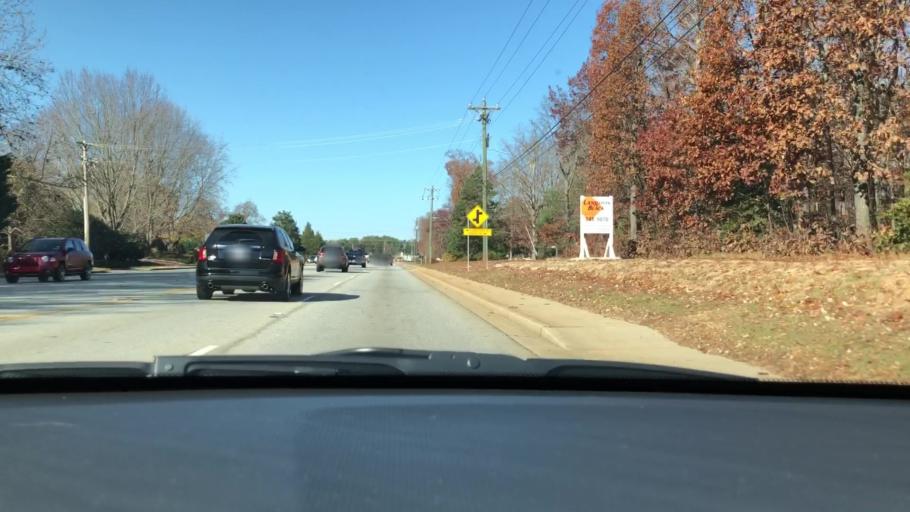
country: US
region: South Carolina
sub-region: Greenville County
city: Five Forks
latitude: 34.8110
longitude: -82.2404
